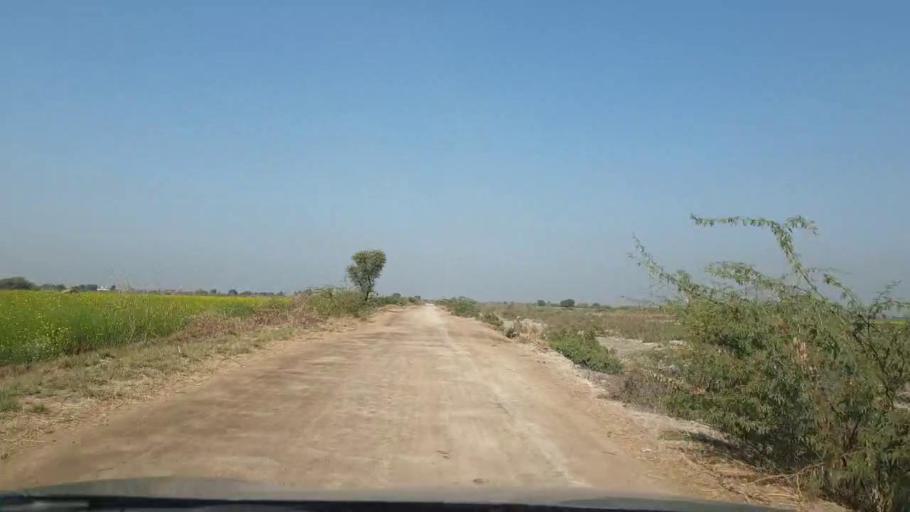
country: PK
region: Sindh
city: Berani
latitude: 25.7163
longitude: 68.8562
